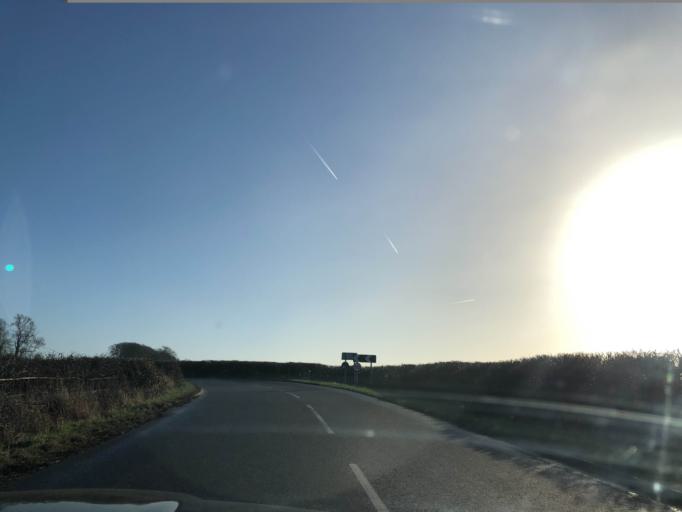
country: GB
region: England
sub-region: Warwickshire
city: Wellesbourne Mountford
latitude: 52.1909
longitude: -1.5693
